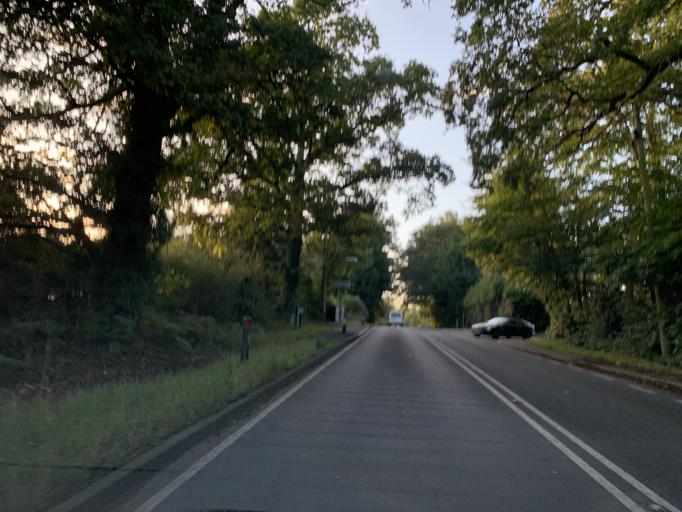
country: GB
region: England
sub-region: Hampshire
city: West Wellow
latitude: 50.9627
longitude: -1.5655
